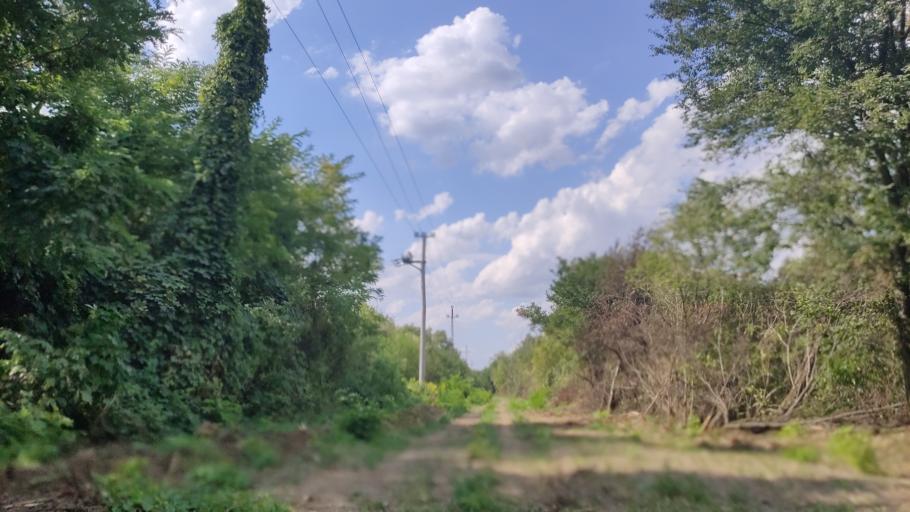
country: HU
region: Pest
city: Biatorbagy
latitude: 47.4659
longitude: 18.8666
